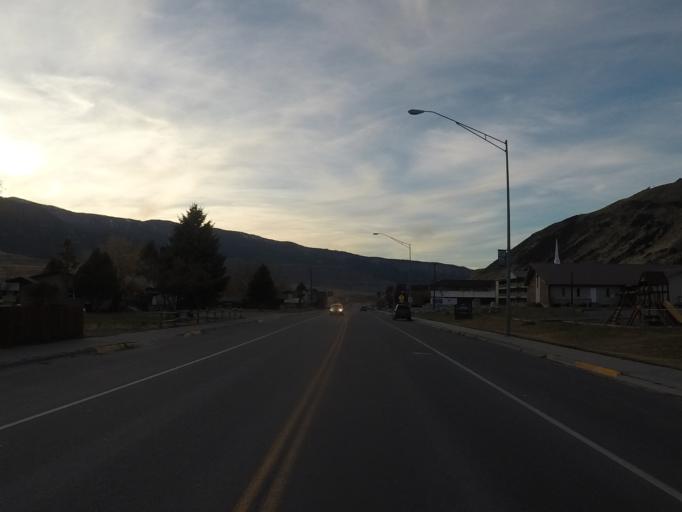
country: US
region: Montana
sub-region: Gallatin County
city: West Yellowstone
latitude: 45.0354
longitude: -110.7126
